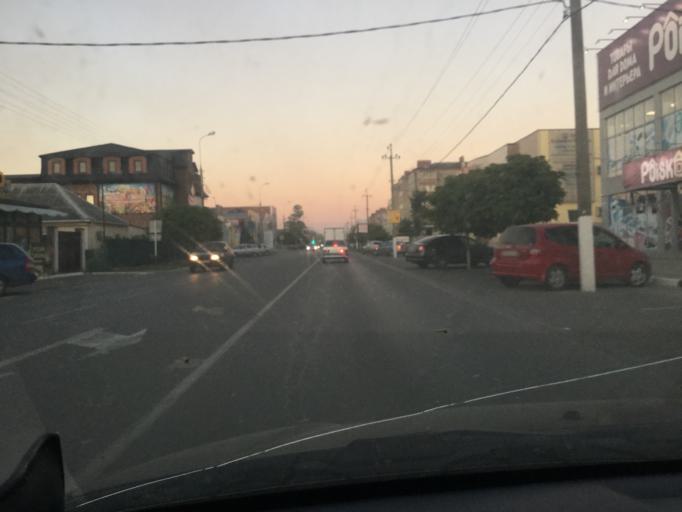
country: RU
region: Krasnodarskiy
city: Slavyansk-na-Kubani
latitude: 45.2575
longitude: 38.1176
